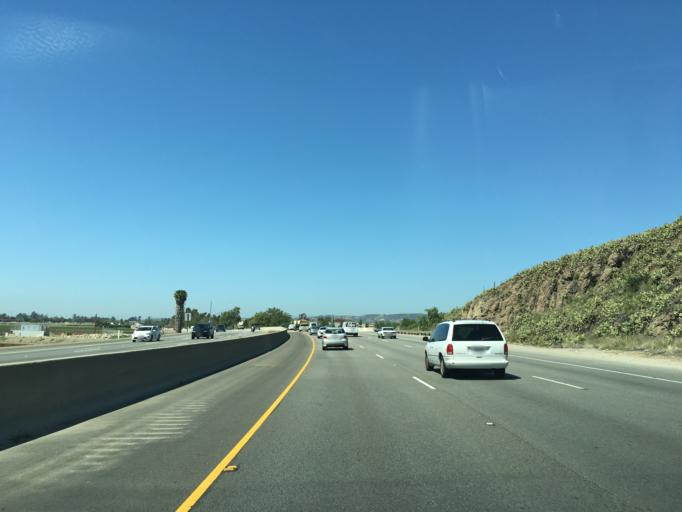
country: US
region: California
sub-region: Ventura County
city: Camarillo
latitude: 34.2082
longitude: -118.9926
